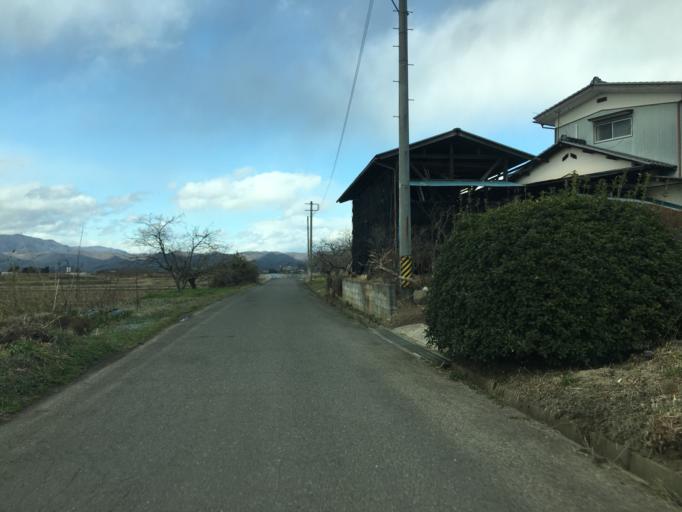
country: JP
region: Fukushima
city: Yanagawamachi-saiwaicho
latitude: 37.8398
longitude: 140.6107
